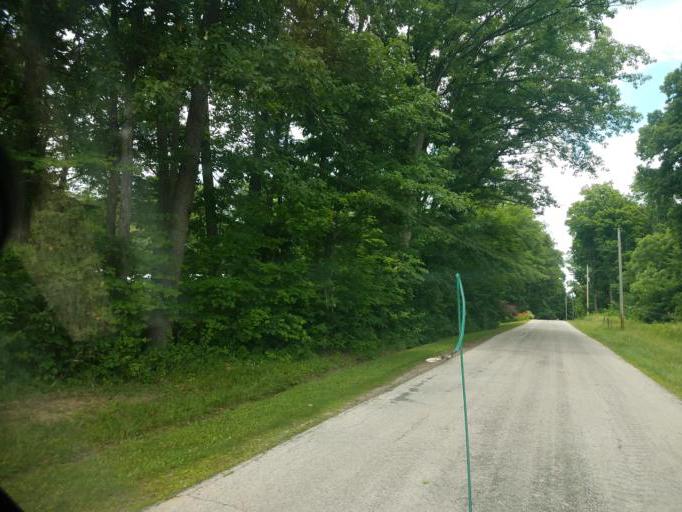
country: US
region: Ohio
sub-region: Huron County
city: Plymouth
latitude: 40.9449
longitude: -82.7050
